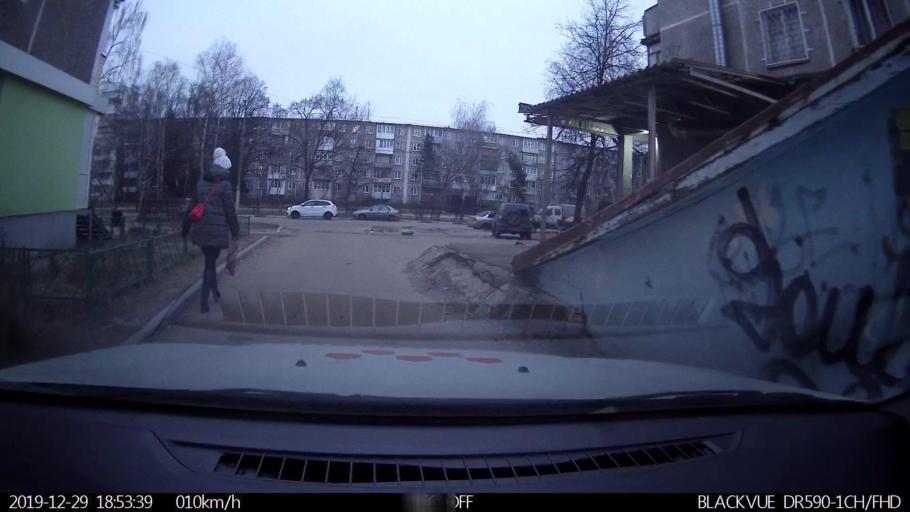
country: RU
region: Nizjnij Novgorod
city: Gorbatovka
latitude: 56.3472
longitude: 43.8522
